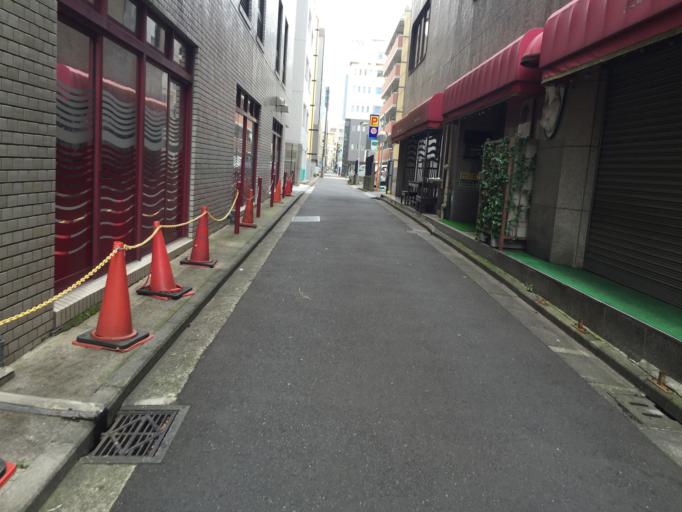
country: JP
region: Kanagawa
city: Yokohama
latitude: 35.4455
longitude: 139.6398
